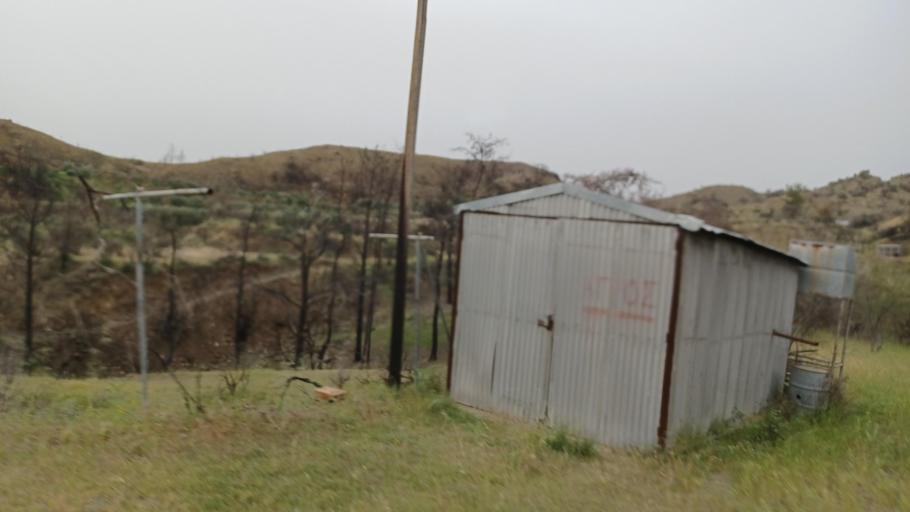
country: CY
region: Limassol
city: Parekklisha
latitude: 34.8522
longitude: 33.1379
